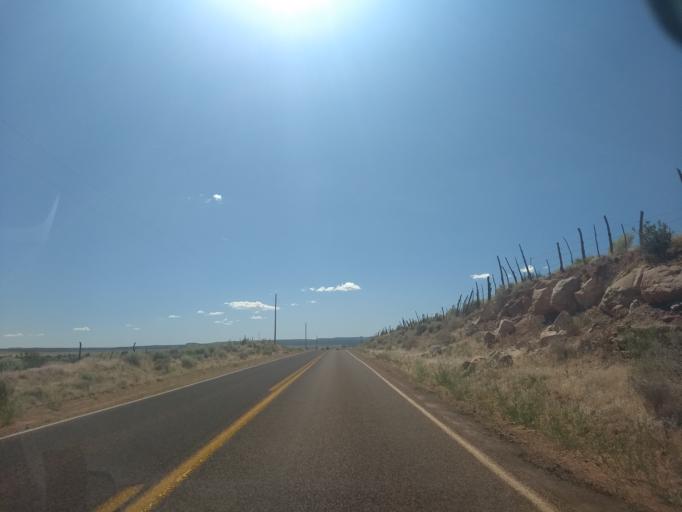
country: US
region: Arizona
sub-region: Mohave County
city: Colorado City
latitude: 36.9469
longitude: -112.9209
